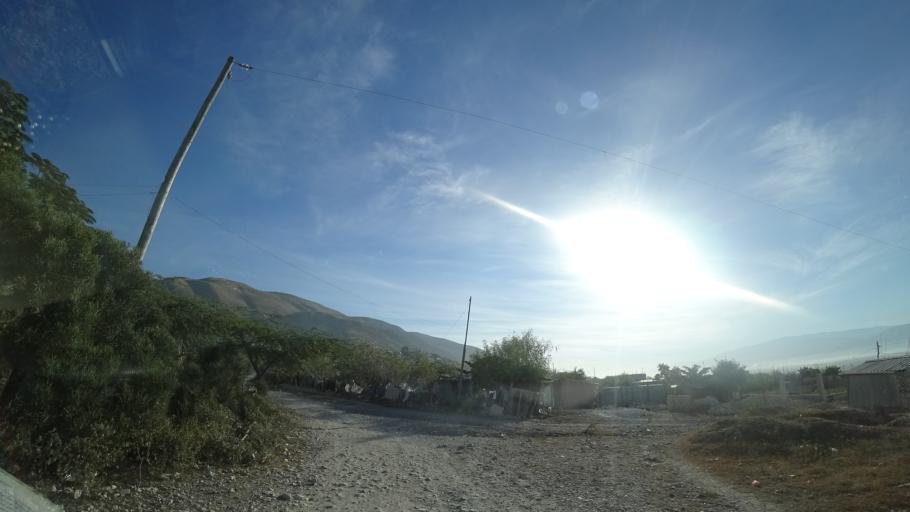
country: HT
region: Ouest
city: Croix des Bouquets
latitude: 18.6696
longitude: -72.2314
